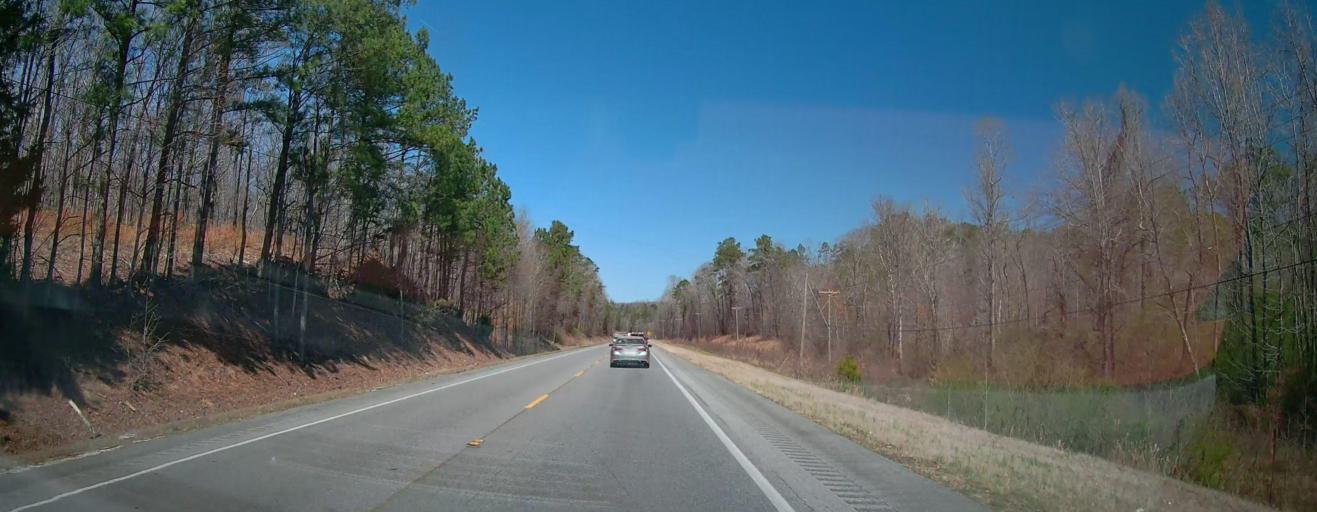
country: US
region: Alabama
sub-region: Calhoun County
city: Ohatchee
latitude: 33.8051
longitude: -86.0363
